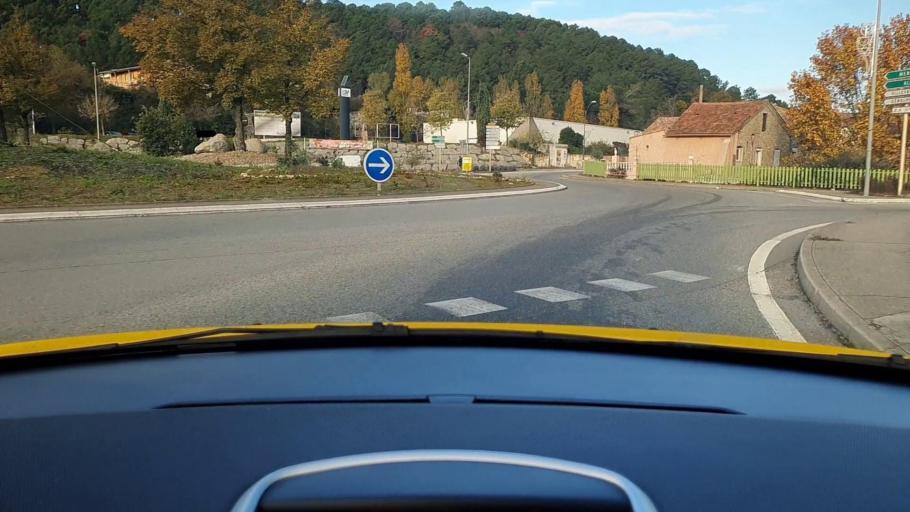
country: FR
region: Languedoc-Roussillon
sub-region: Departement du Gard
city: Saint-Martin-de-Valgalgues
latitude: 44.1571
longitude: 4.0844
